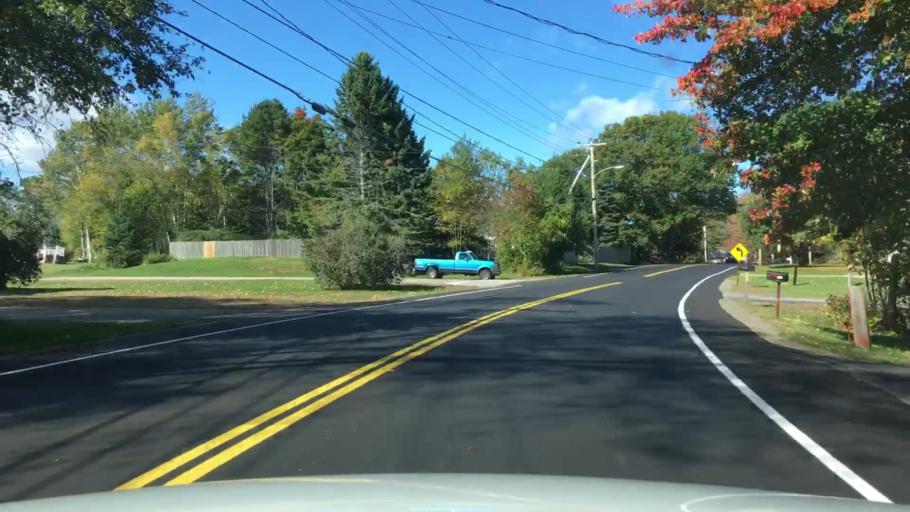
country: US
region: Maine
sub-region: York County
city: Biddeford
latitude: 43.4603
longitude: -70.4351
